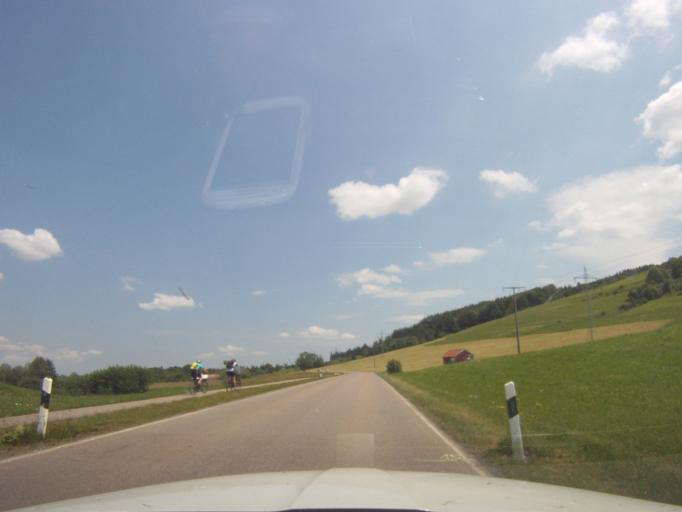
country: DE
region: Bavaria
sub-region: Swabia
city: Oy-Mittelberg
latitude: 47.6053
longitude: 10.4392
